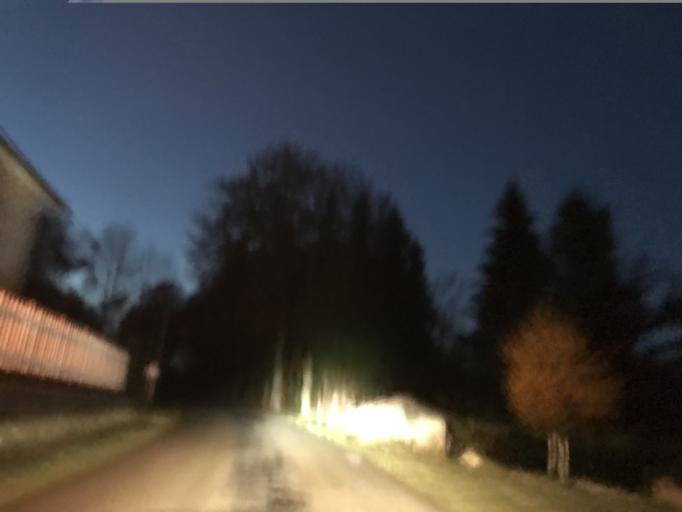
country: FR
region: Rhone-Alpes
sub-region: Departement de la Loire
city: Noiretable
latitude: 45.7242
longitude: 3.7395
